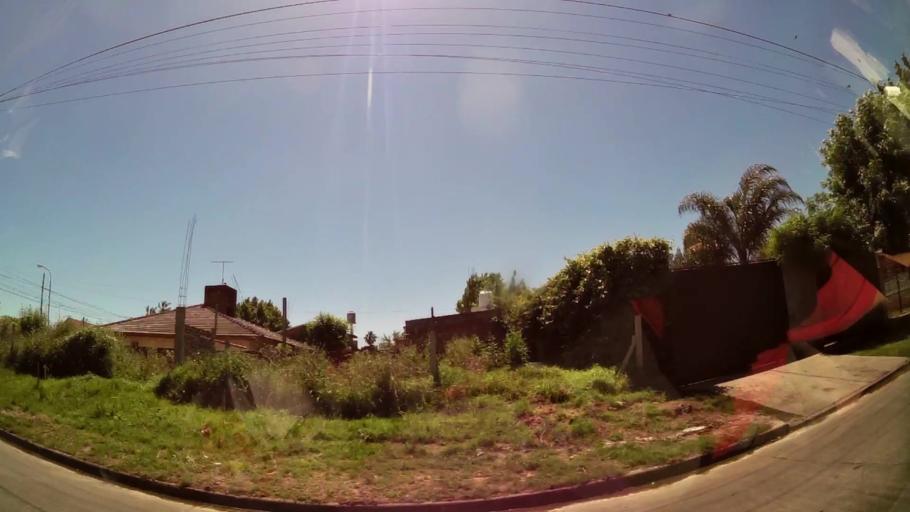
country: AR
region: Buenos Aires
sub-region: Partido de Tigre
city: Tigre
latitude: -34.4845
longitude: -58.6366
